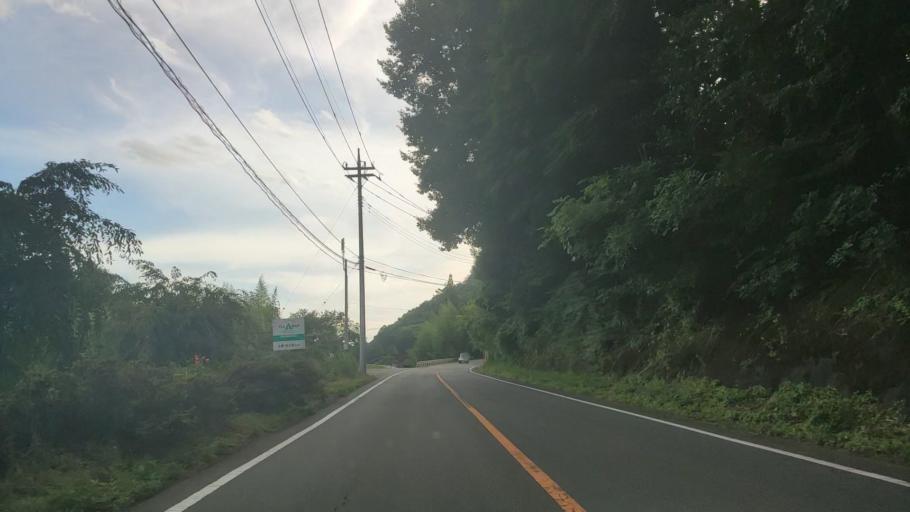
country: JP
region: Gunma
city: Omamacho-omama
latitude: 36.5258
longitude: 139.3116
